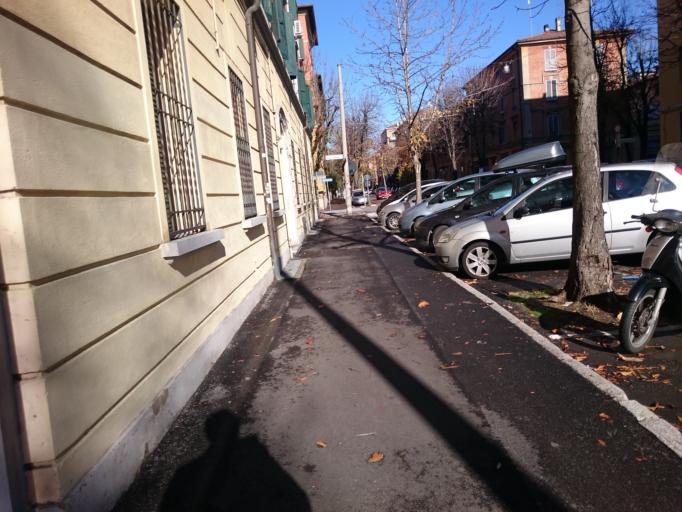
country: IT
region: Emilia-Romagna
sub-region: Provincia di Bologna
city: Bologna
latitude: 44.5101
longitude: 11.3428
